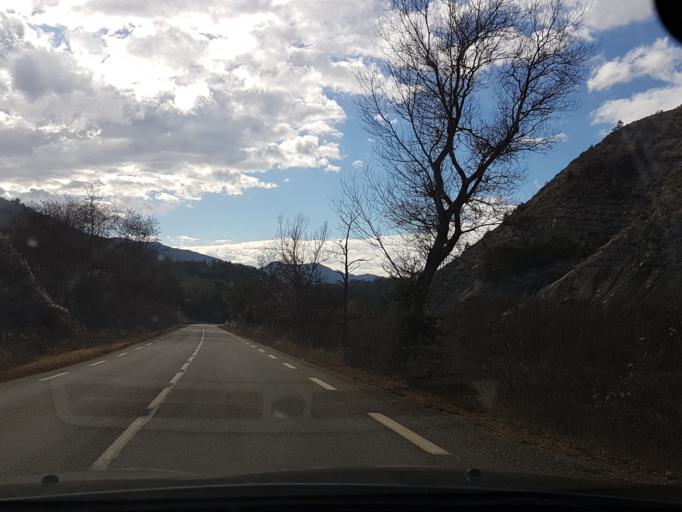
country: FR
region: Provence-Alpes-Cote d'Azur
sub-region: Departement des Hautes-Alpes
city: Tallard
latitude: 44.4965
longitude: 6.0825
